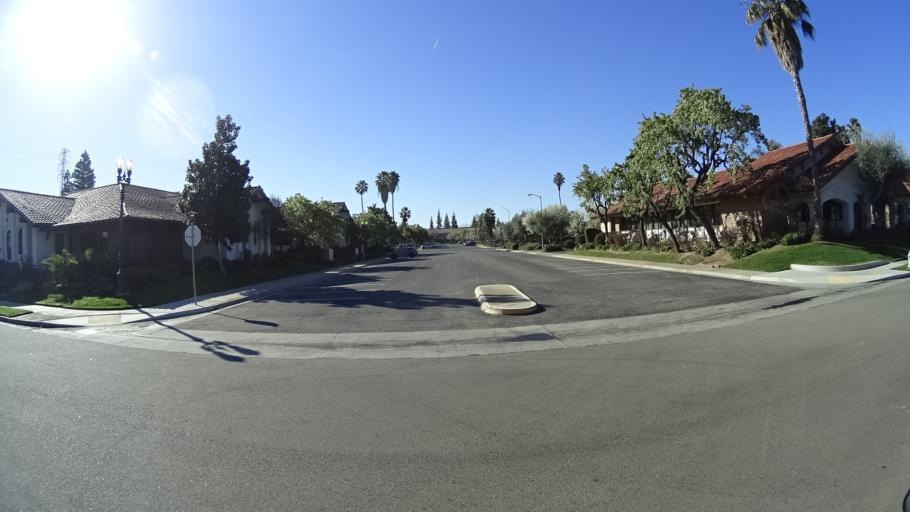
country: US
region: California
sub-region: Fresno County
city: Clovis
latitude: 36.8406
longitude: -119.7711
